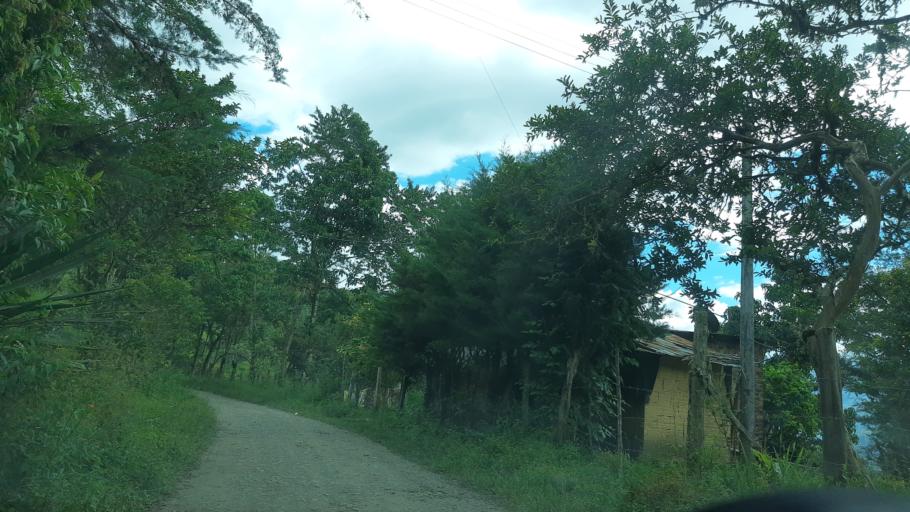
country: CO
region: Boyaca
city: Garagoa
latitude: 5.0411
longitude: -73.3344
